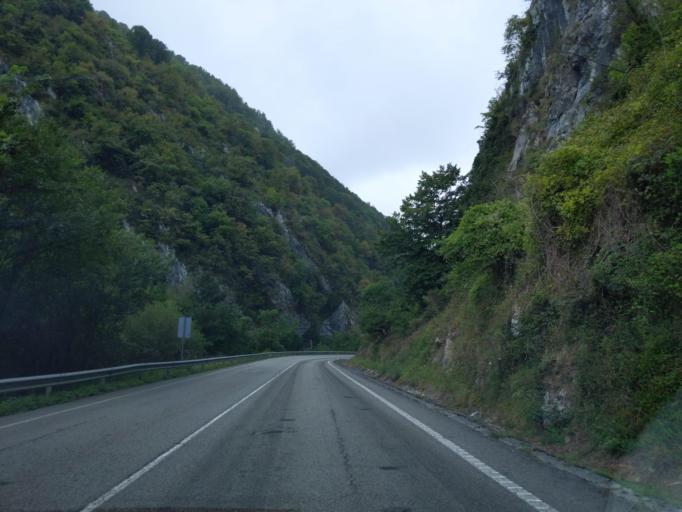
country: ES
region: Asturias
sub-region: Province of Asturias
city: Pola de Laviana
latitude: 43.2325
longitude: -5.4860
